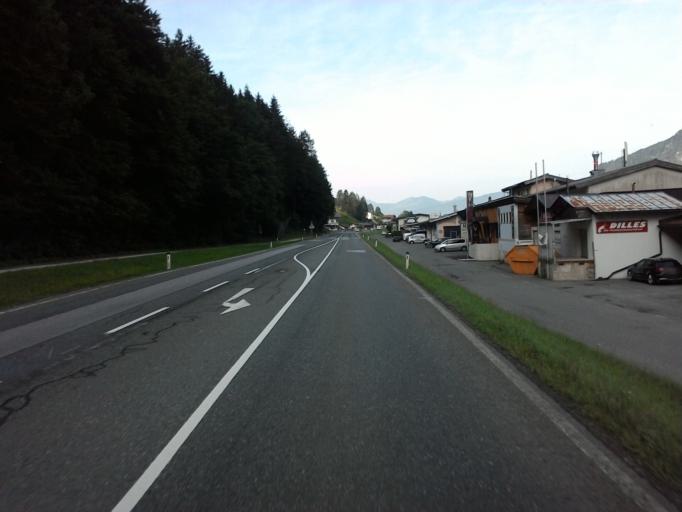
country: AT
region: Tyrol
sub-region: Politischer Bezirk Kitzbuhel
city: Kirchdorf in Tirol
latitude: 47.5586
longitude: 12.4604
